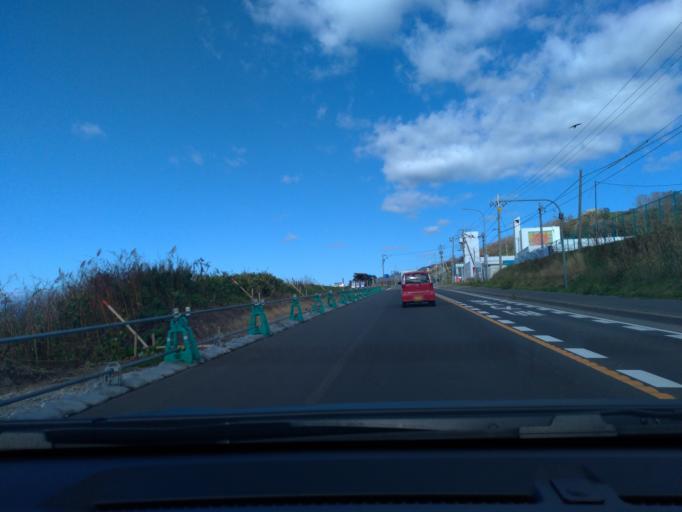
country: JP
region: Hokkaido
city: Ishikari
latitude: 43.4017
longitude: 141.4316
